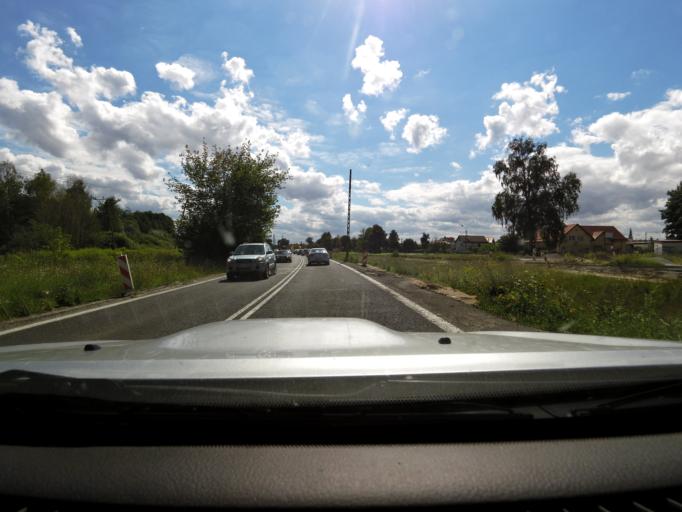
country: PL
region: Warmian-Masurian Voivodeship
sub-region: Powiat ostrodzki
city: Ostroda
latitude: 53.7193
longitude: 19.9483
